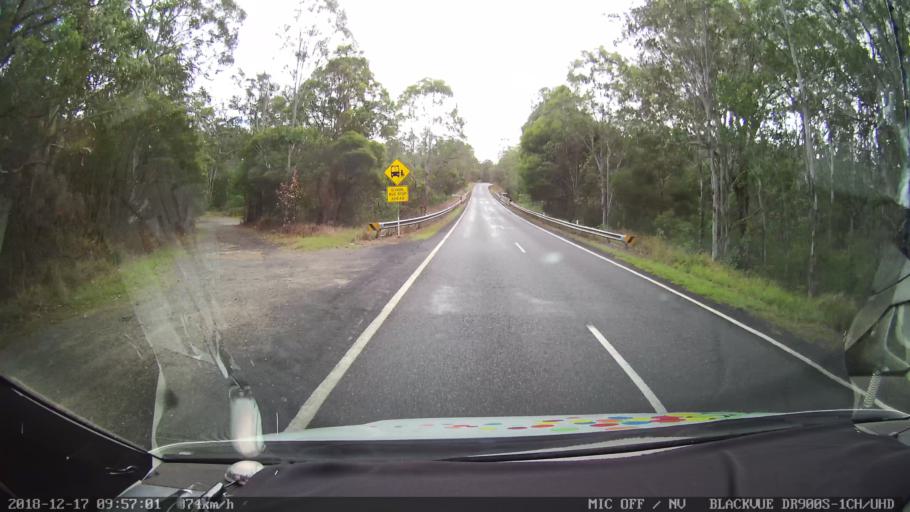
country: AU
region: New South Wales
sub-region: Tenterfield Municipality
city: Carrolls Creek
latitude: -28.9286
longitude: 152.3935
